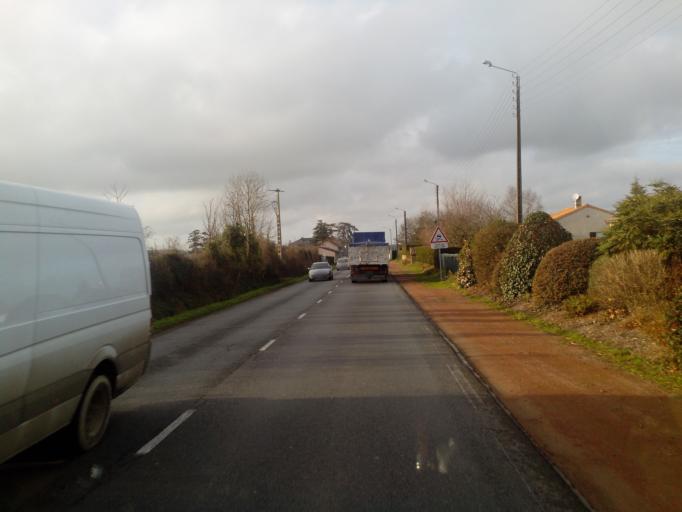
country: FR
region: Poitou-Charentes
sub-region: Departement des Deux-Sevres
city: Chiche
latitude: 46.7946
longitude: -0.3530
